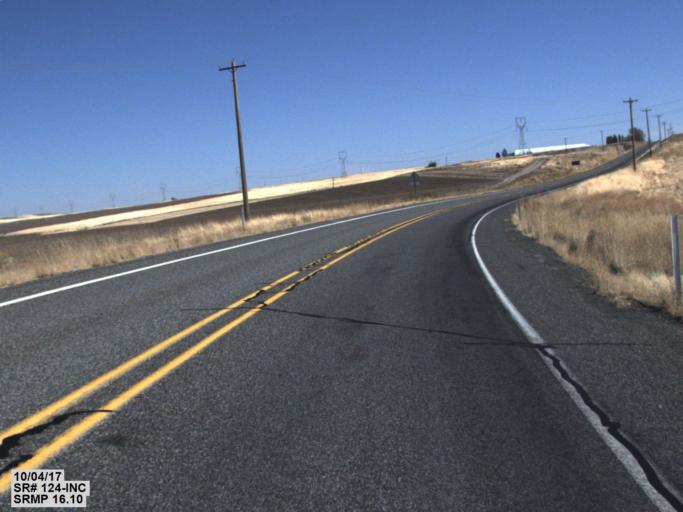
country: US
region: Washington
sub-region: Walla Walla County
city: Burbank
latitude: 46.2977
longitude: -118.7196
